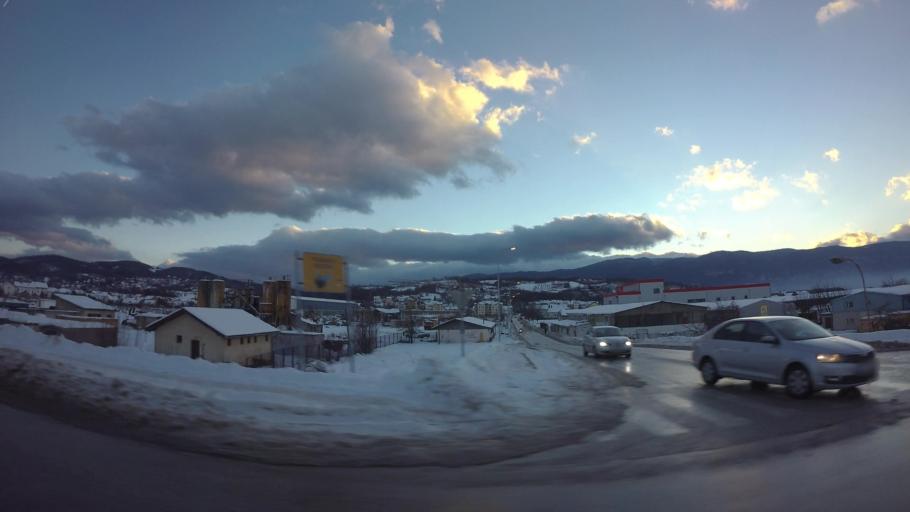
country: BA
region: Federation of Bosnia and Herzegovina
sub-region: Kanton Sarajevo
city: Sarajevo
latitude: 43.8146
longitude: 18.3651
